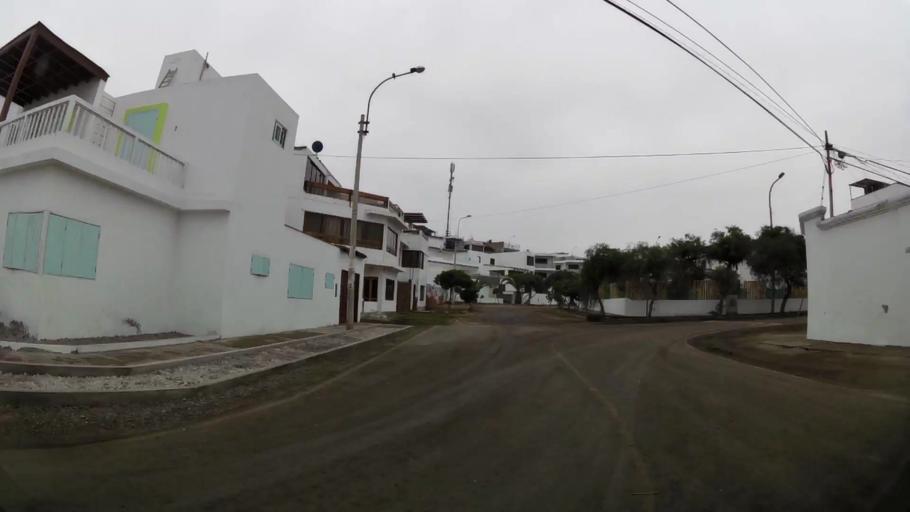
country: PE
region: Lima
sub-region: Lima
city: Punta Hermosa
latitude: -12.3354
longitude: -76.8281
